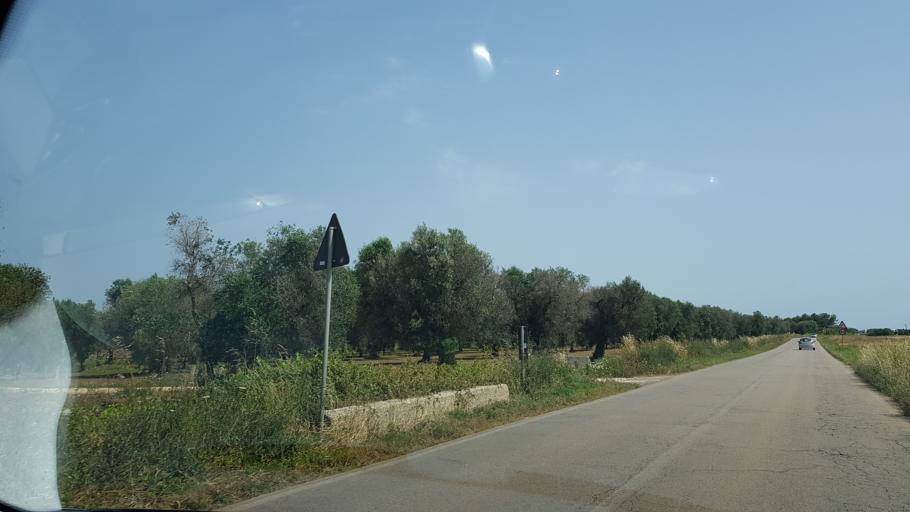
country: IT
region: Apulia
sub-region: Provincia di Lecce
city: Porto Cesareo
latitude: 40.3317
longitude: 17.8519
